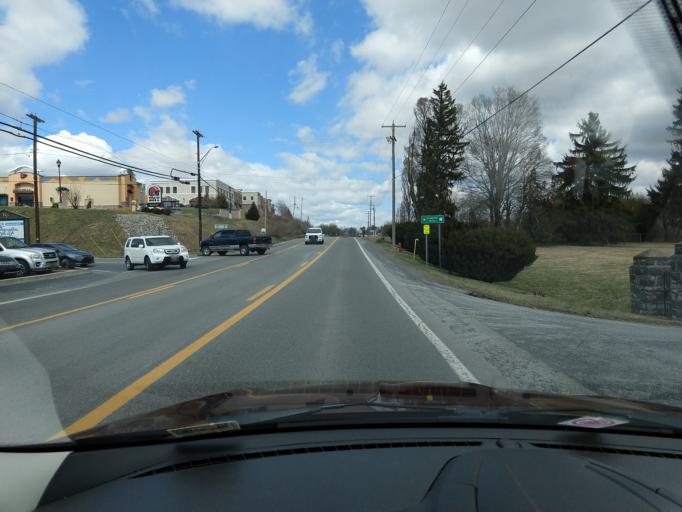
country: US
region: West Virginia
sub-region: Greenbrier County
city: Lewisburg
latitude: 37.8098
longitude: -80.4341
